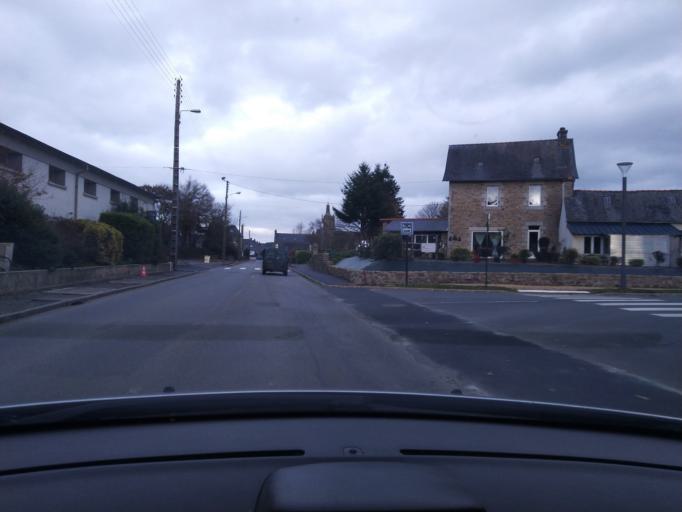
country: FR
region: Brittany
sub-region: Departement des Cotes-d'Armor
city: Plouaret
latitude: 48.6097
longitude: -3.4762
